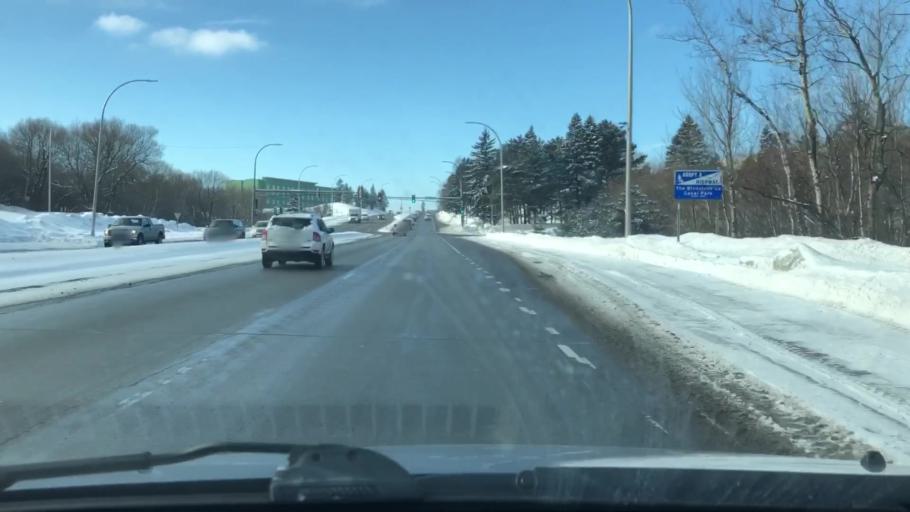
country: US
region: Minnesota
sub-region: Saint Louis County
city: Duluth
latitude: 46.7994
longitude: -92.1147
